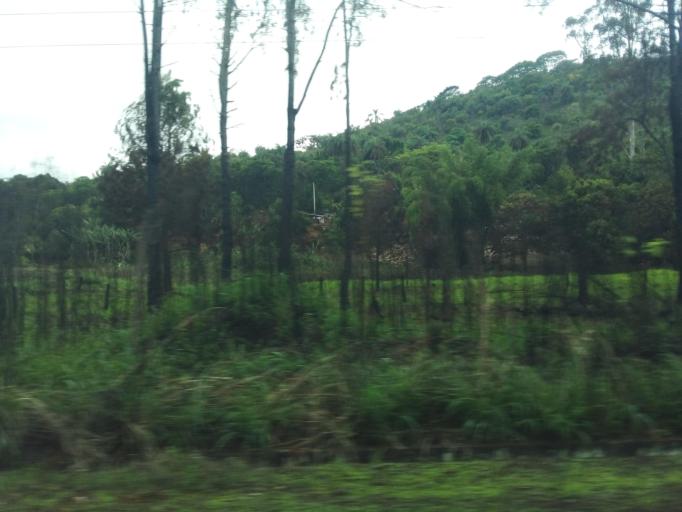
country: BR
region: Minas Gerais
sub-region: Rio Piracicaba
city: Rio Piracicaba
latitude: -19.9621
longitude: -43.2715
